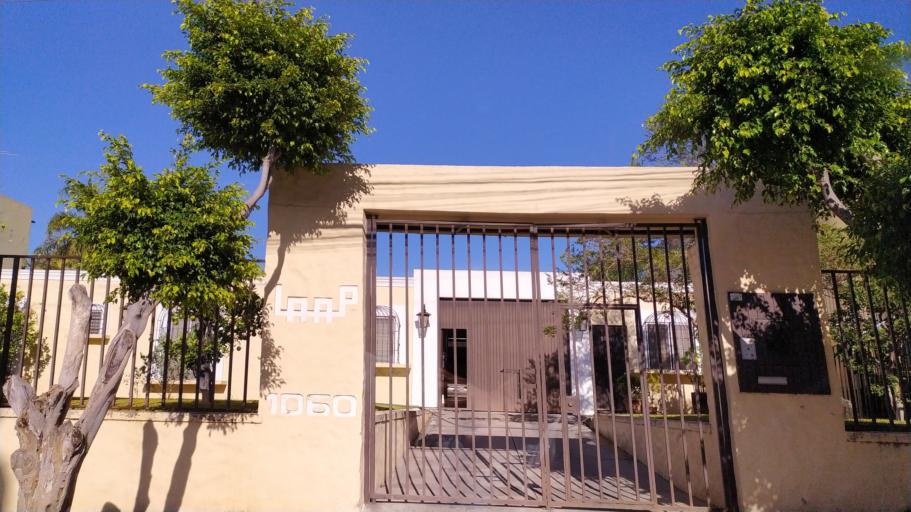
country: MX
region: Jalisco
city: Guadalajara
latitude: 20.6561
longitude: -103.4258
